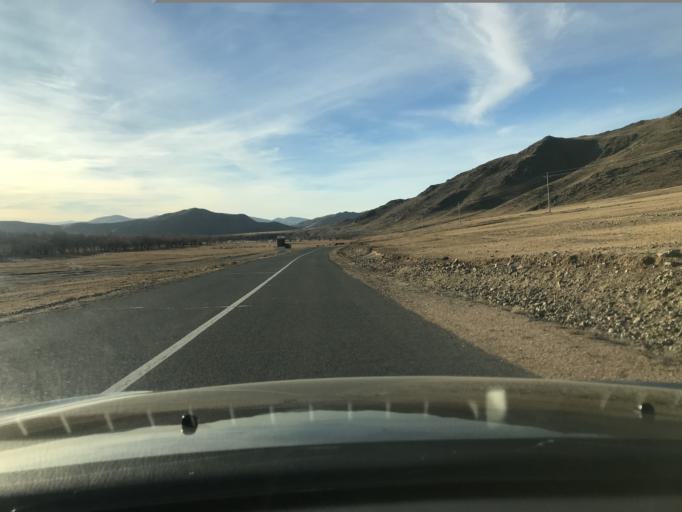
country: MN
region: Central Aimak
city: Dzuunmod
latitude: 47.8221
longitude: 107.3588
